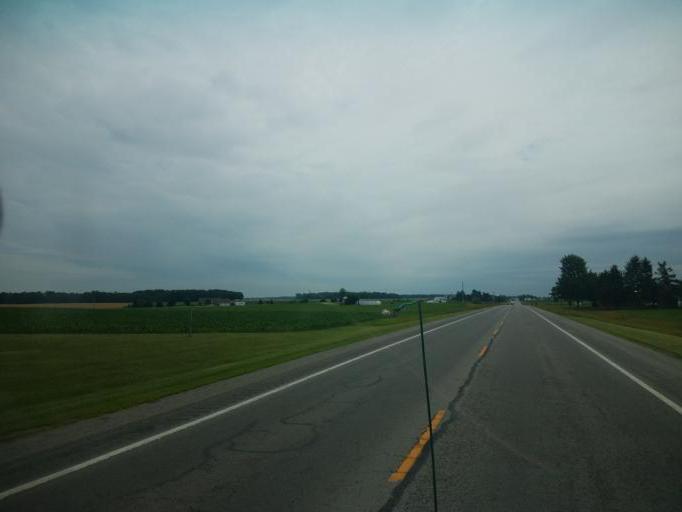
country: US
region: Ohio
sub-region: Hardin County
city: Kenton
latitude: 40.6814
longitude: -83.6783
